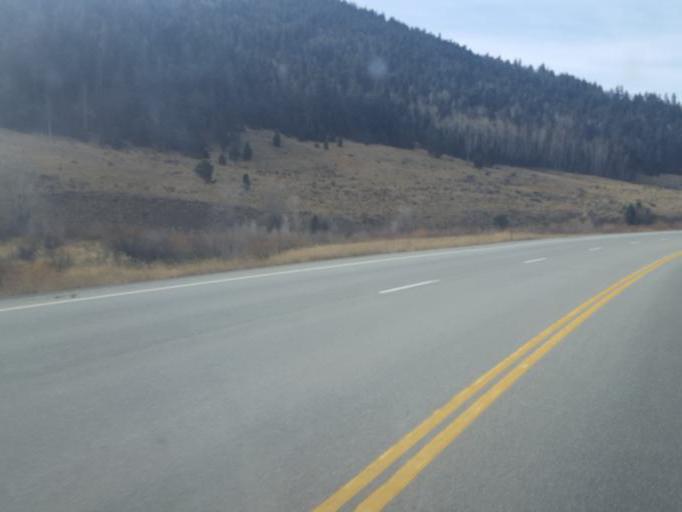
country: US
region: Colorado
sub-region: Costilla County
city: San Luis
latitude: 37.6026
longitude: -105.2303
